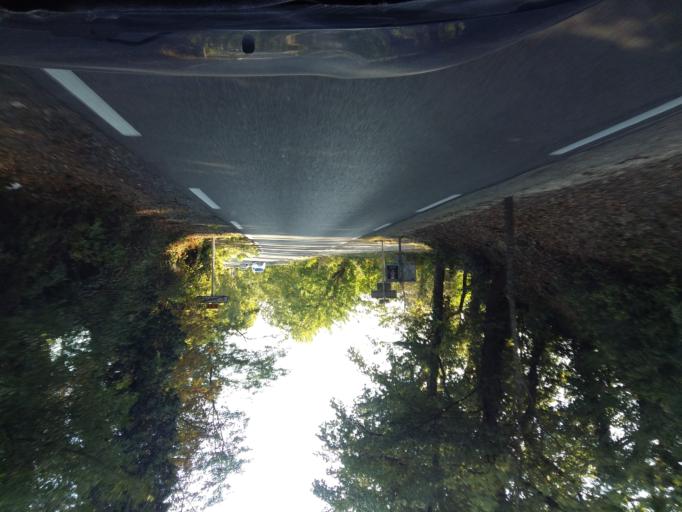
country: FR
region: Provence-Alpes-Cote d'Azur
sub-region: Departement du Vaucluse
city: Saint-Didier
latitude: 44.0110
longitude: 5.1048
